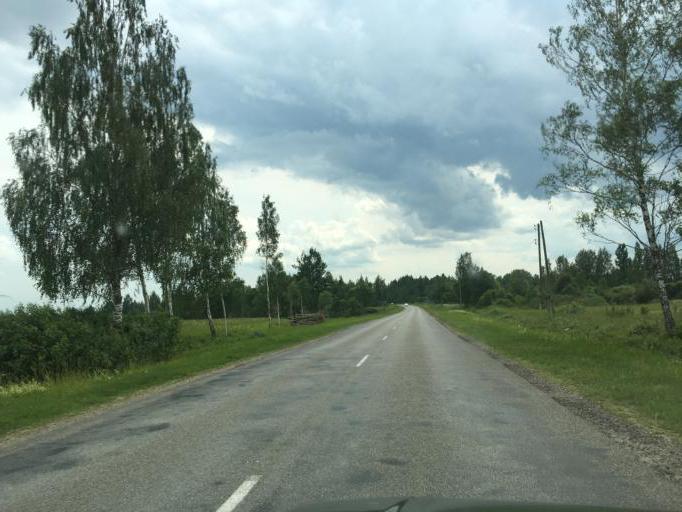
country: LV
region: Rugaju
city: Rugaji
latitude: 56.9406
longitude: 27.0676
